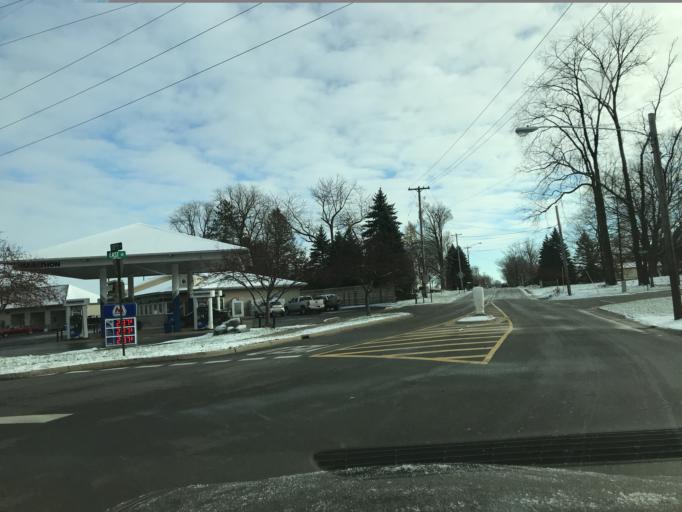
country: US
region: Michigan
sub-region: Eaton County
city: Dimondale
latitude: 42.6474
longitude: -84.6427
